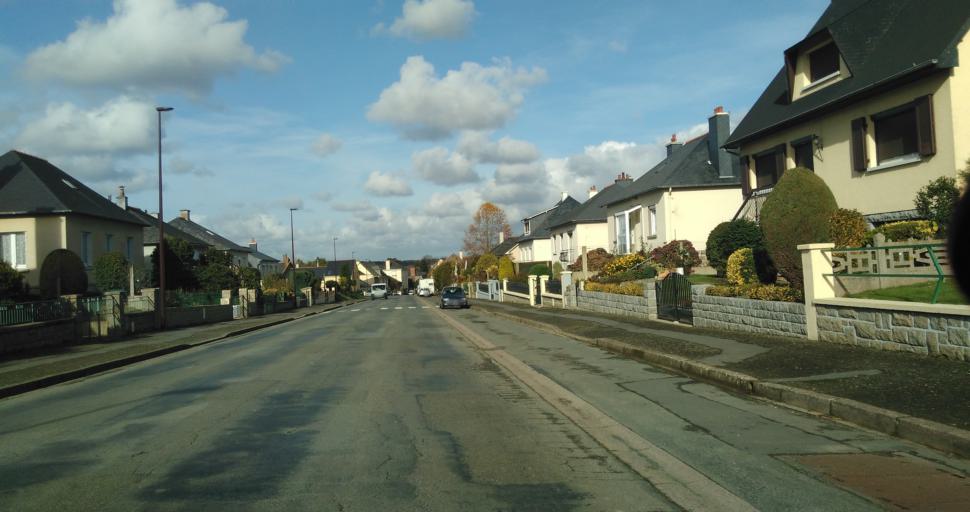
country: FR
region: Brittany
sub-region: Departement d'Ille-et-Vilaine
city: Montauban-de-Bretagne
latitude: 48.1867
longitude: -2.0507
